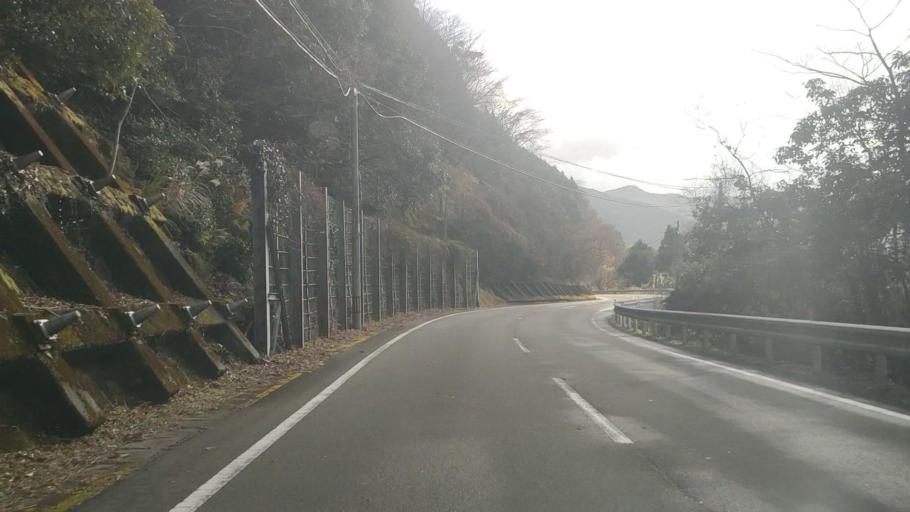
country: JP
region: Kumamoto
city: Hitoyoshi
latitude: 32.3217
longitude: 130.8400
